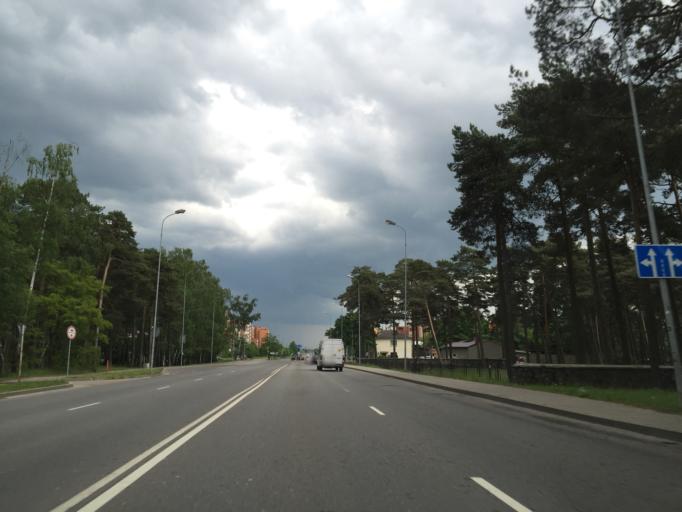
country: LT
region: Klaipedos apskritis
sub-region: Klaipeda
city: Klaipeda
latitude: 55.7315
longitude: 21.1216
